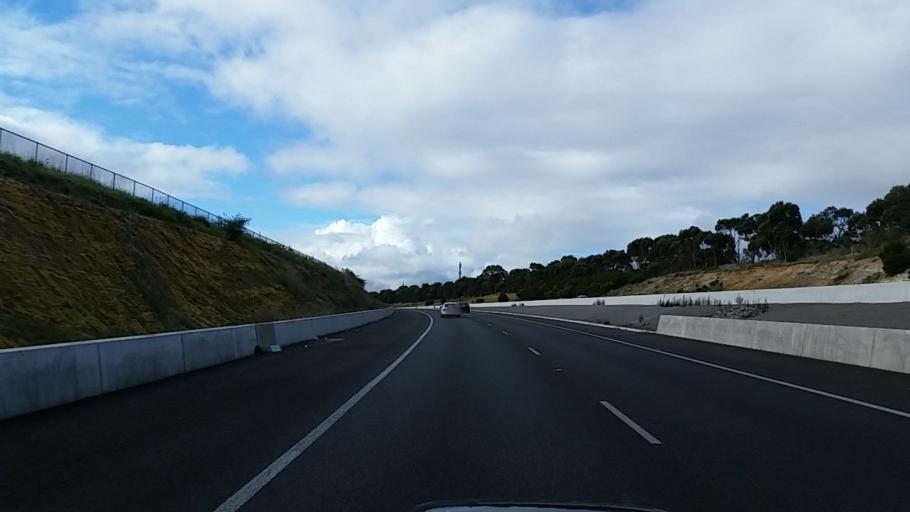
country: AU
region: South Australia
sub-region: Marion
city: Happy Valley
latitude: -35.0865
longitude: 138.5402
